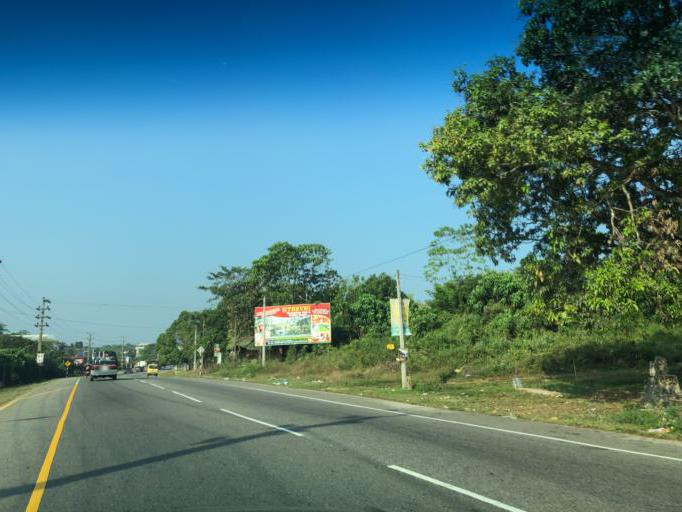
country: LK
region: Western
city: Horana South
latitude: 6.7317
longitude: 80.1085
